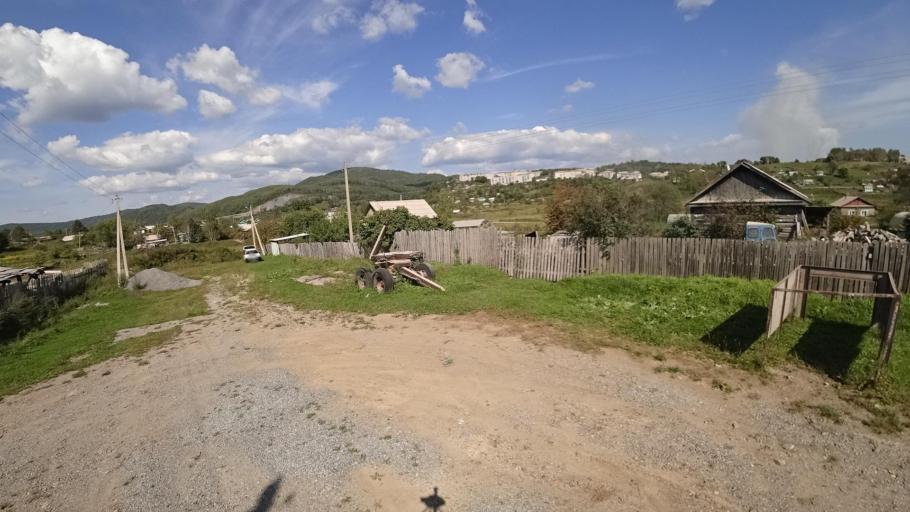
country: RU
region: Jewish Autonomous Oblast
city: Londoko
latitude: 49.0094
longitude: 131.8718
